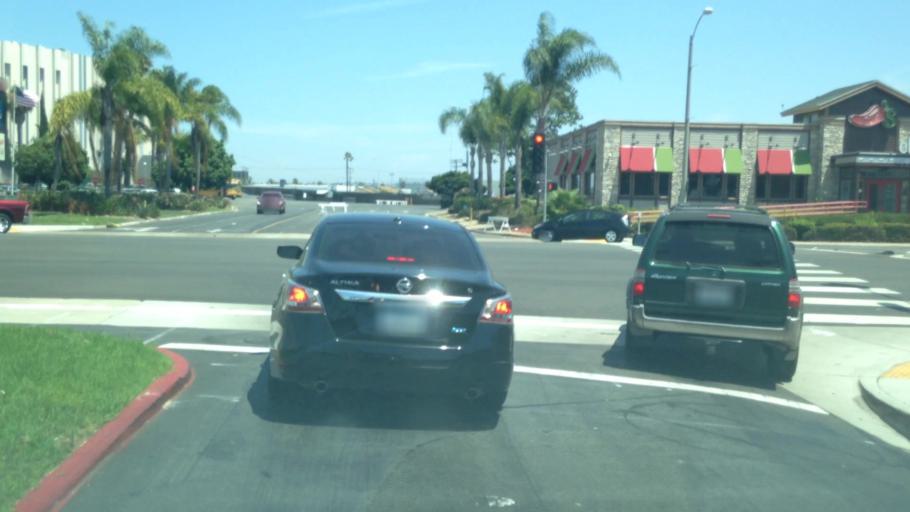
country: US
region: California
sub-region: San Diego County
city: San Diego
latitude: 32.7534
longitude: -117.2115
